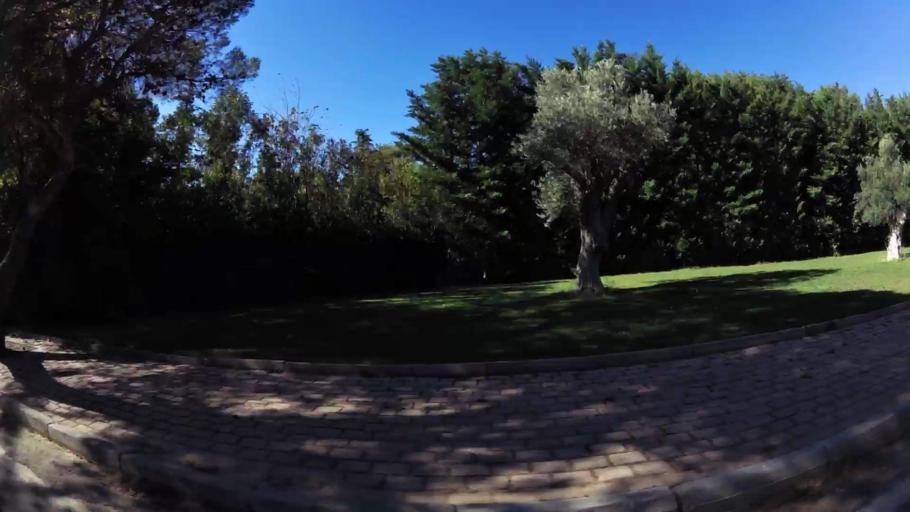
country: GR
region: Attica
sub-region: Nomarchia Anatolikis Attikis
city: Varybobi
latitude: 38.1231
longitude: 23.7965
